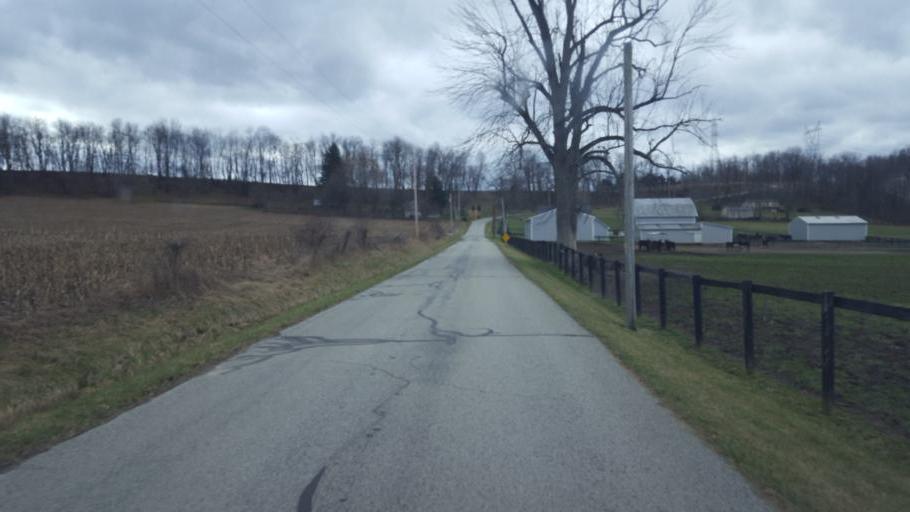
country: US
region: Ohio
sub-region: Licking County
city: Utica
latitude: 40.2131
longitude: -82.3886
